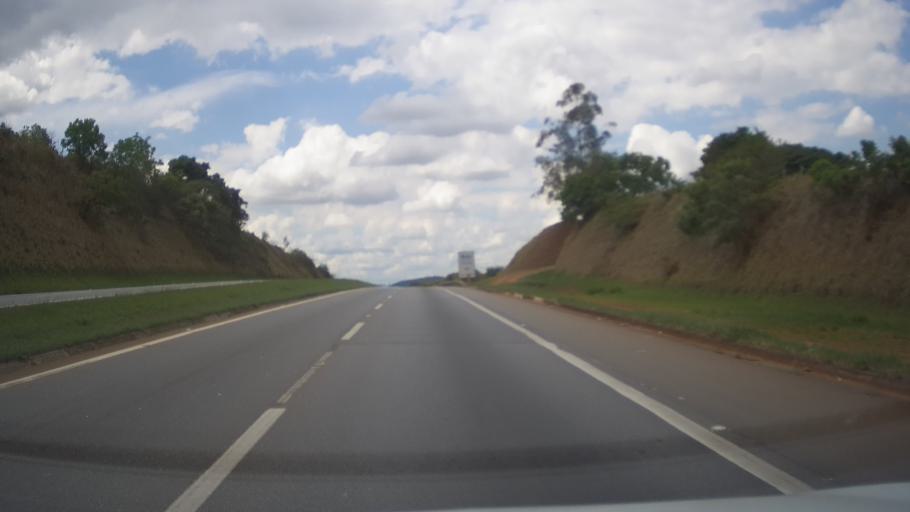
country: BR
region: Minas Gerais
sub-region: Nepomuceno
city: Nepomuceno
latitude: -21.2465
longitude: -45.1375
